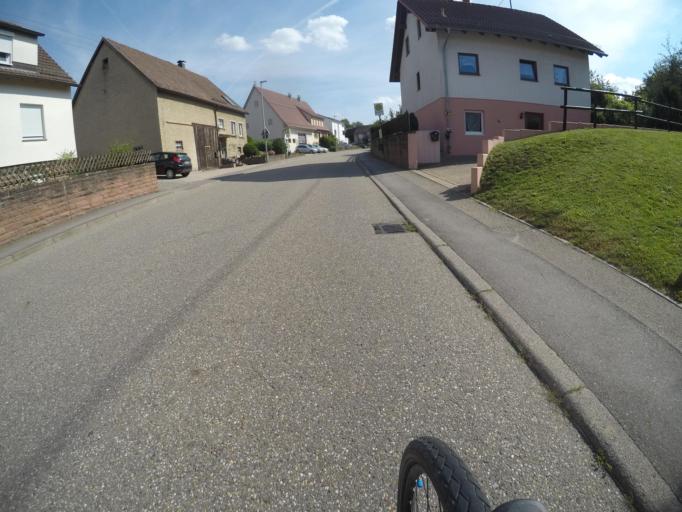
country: DE
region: Baden-Wuerttemberg
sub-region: Karlsruhe Region
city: Olbronn-Durrn
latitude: 48.9789
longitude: 8.7543
